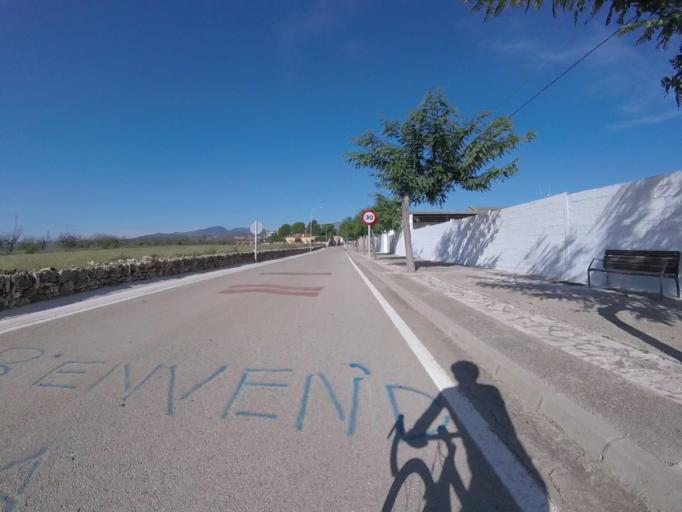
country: ES
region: Valencia
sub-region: Provincia de Castello
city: Sarratella
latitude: 40.2617
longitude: 0.0740
